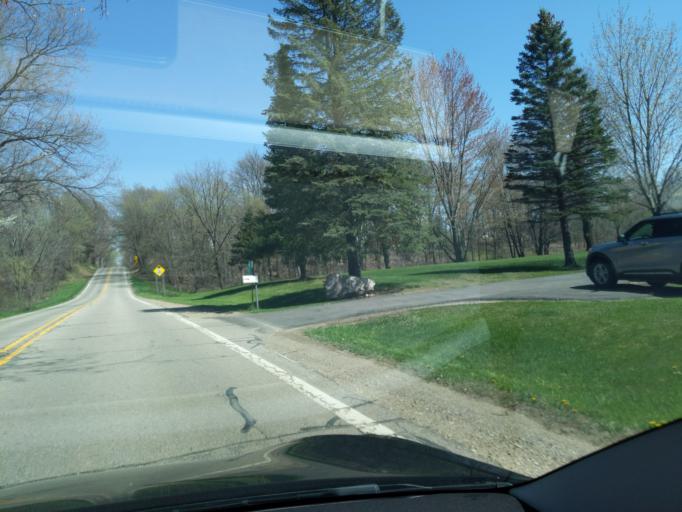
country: US
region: Michigan
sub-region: Ingham County
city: Stockbridge
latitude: 42.4462
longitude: -84.0974
